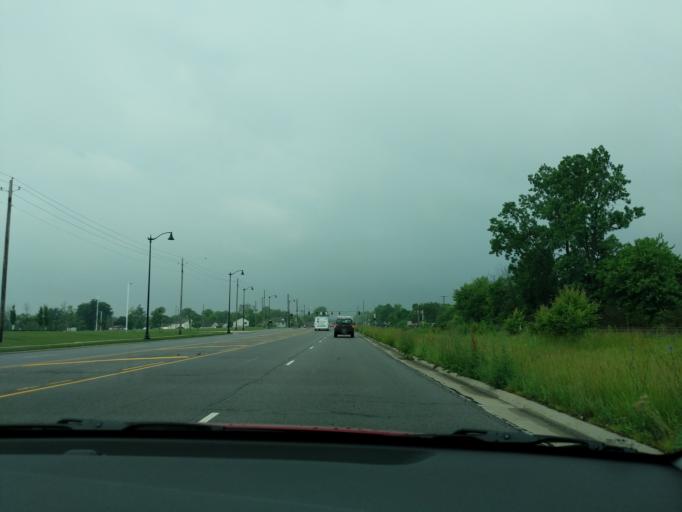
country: US
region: Indiana
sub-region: Hancock County
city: McCordsville
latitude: 39.8881
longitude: -85.9358
